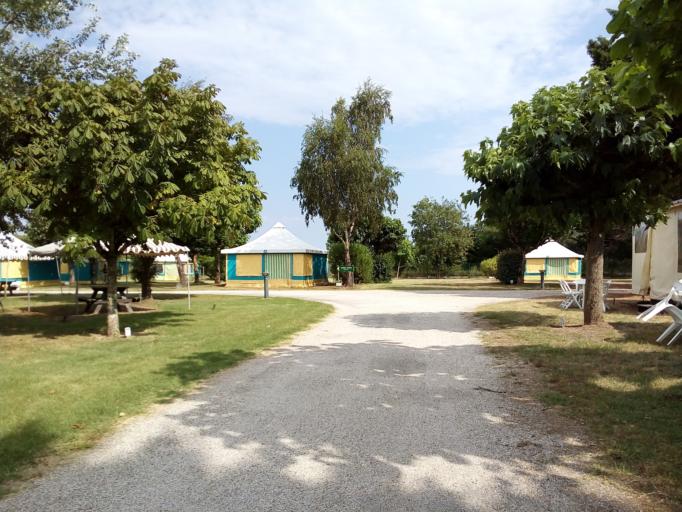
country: FR
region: Poitou-Charentes
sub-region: Departement de la Charente-Maritime
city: Boyard-Ville
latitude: 45.9491
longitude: -1.2468
